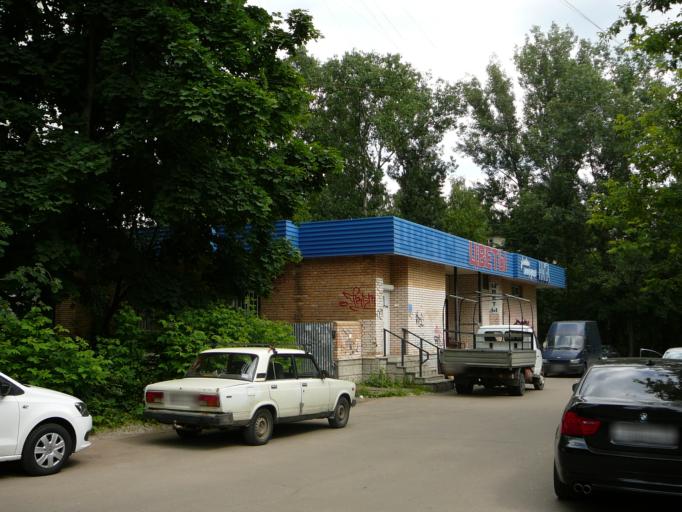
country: RU
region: Moskovskaya
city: Krasnogorsk
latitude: 55.8134
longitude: 37.3088
